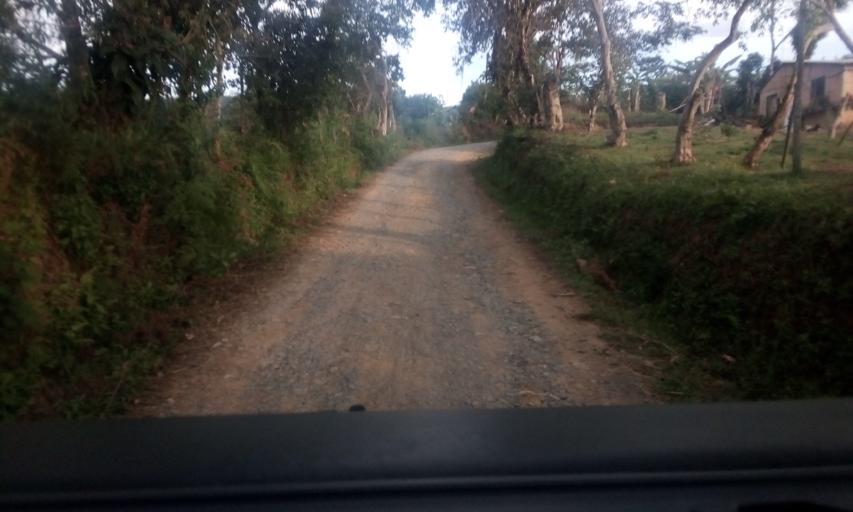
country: CO
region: Boyaca
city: Santana
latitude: 6.0132
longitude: -73.5101
